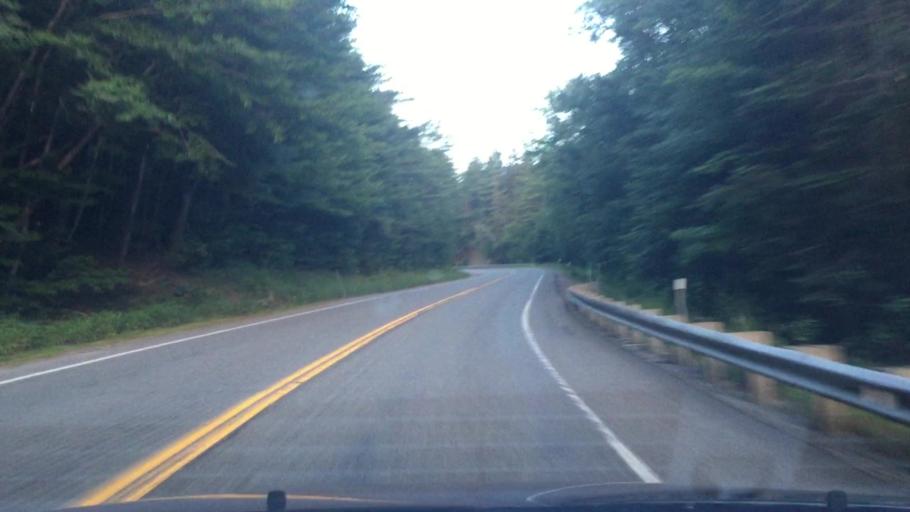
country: US
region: New Hampshire
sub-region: Grafton County
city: Woodstock
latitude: 44.0391
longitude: -71.5400
